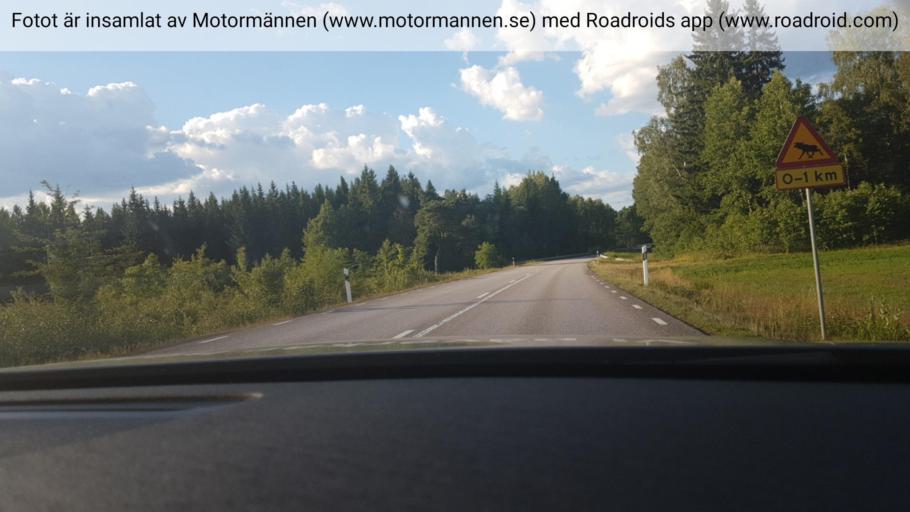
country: SE
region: Vaestra Goetaland
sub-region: Tidaholms Kommun
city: Tidaholm
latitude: 58.0707
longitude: 13.8618
